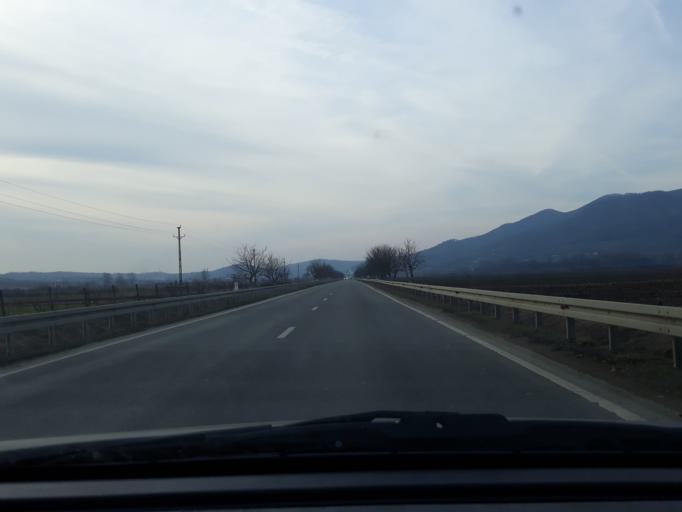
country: RO
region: Salaj
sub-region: Comuna Periceiu
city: Periceiu
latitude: 47.2280
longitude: 22.8496
